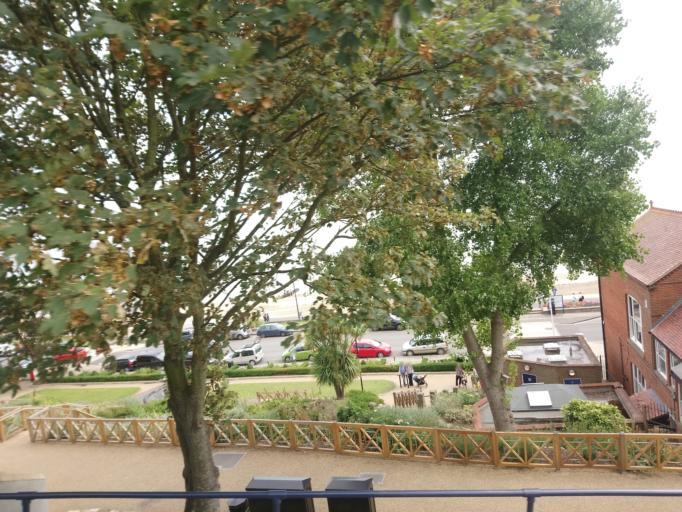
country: GB
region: England
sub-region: Suffolk
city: Felixstowe
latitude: 51.9595
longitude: 1.3482
